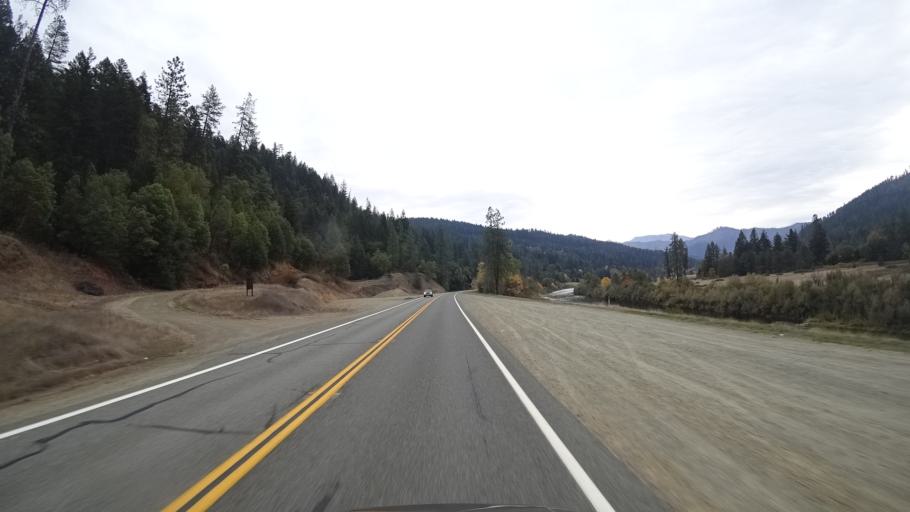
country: US
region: California
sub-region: Siskiyou County
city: Happy Camp
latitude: 41.8111
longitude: -123.3542
